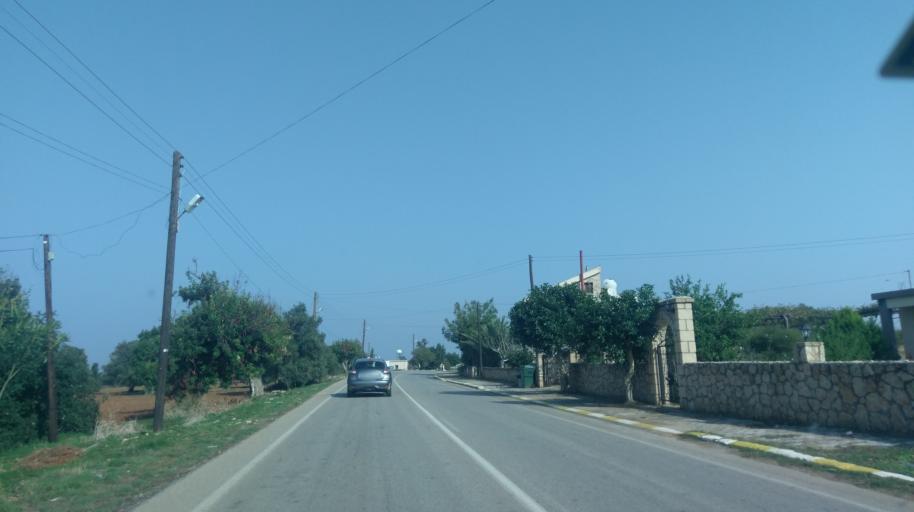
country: CY
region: Ammochostos
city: Leonarisso
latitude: 35.5239
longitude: 34.1765
